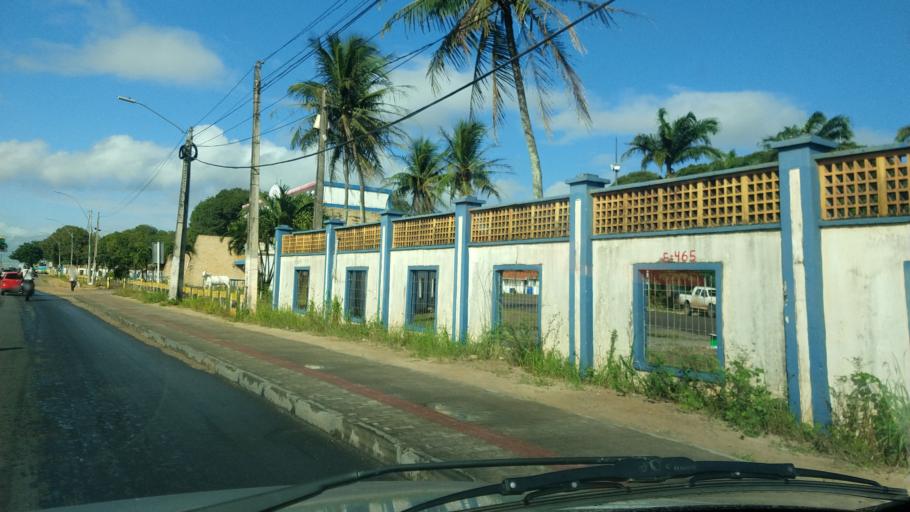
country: BR
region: Rio Grande do Norte
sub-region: Parnamirim
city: Parnamirim
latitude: -5.9040
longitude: -35.2602
